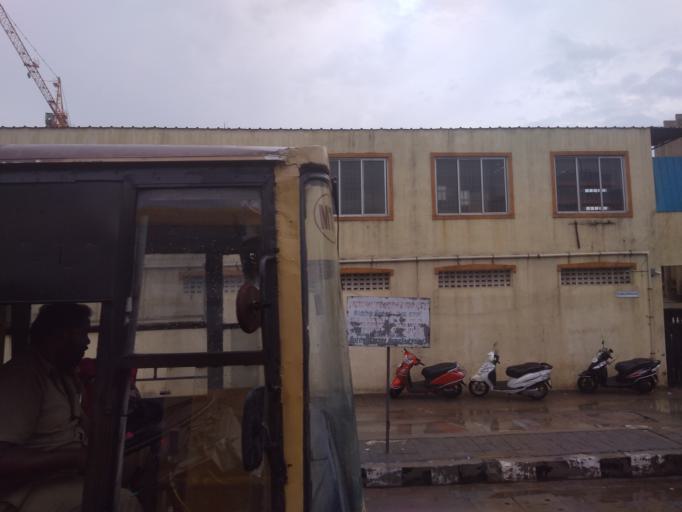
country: IN
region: Tamil Nadu
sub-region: Kancheepuram
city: Perungudi
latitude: 12.9513
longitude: 80.2412
